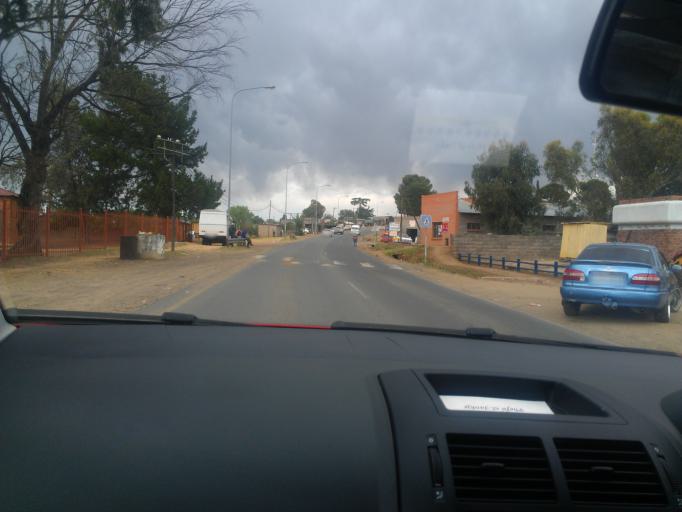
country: LS
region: Berea
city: Teyateyaneng
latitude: -29.1511
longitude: 27.7462
